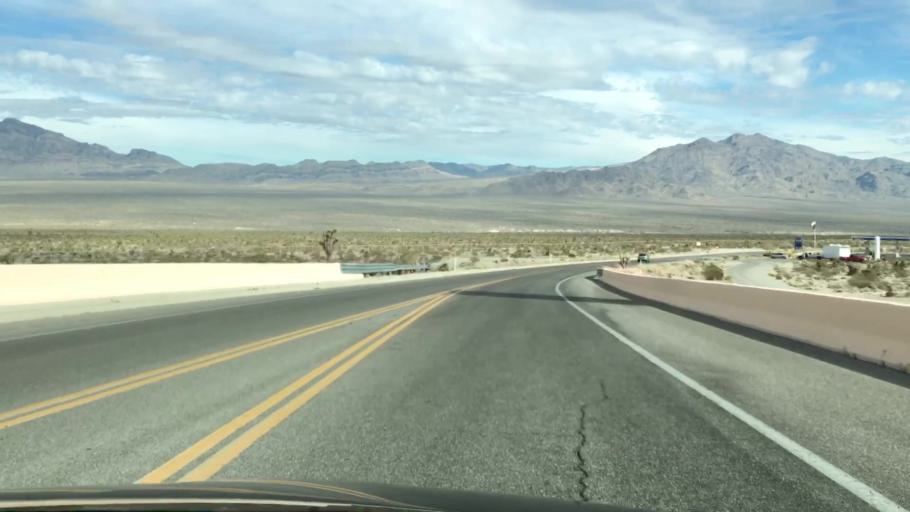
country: US
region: Nevada
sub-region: Clark County
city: Summerlin South
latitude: 36.3636
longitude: -115.3490
